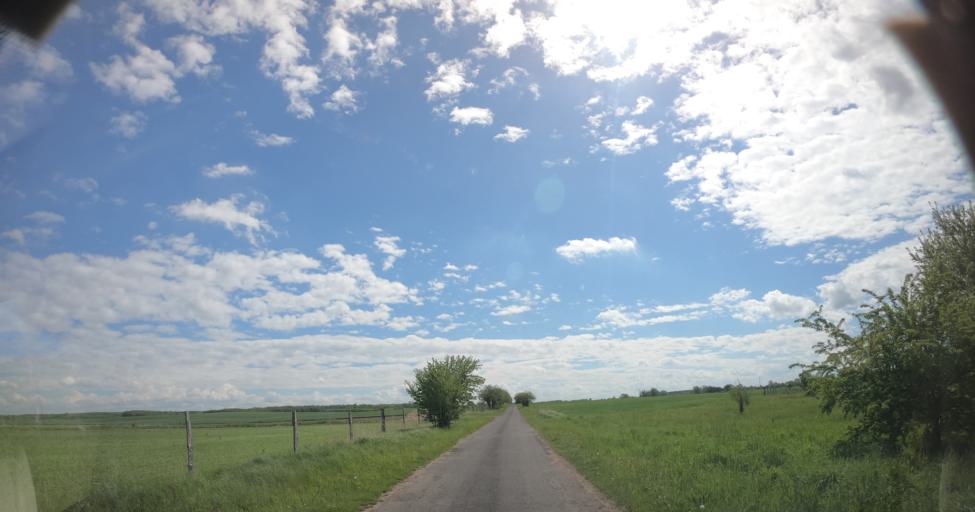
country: PL
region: West Pomeranian Voivodeship
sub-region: Powiat stargardzki
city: Dobrzany
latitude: 53.3525
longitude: 15.4398
